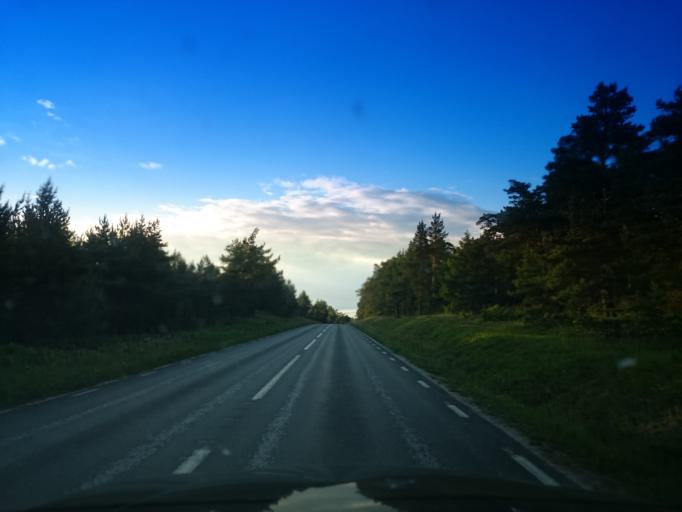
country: SE
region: Gotland
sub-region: Gotland
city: Hemse
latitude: 57.3353
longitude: 18.3788
